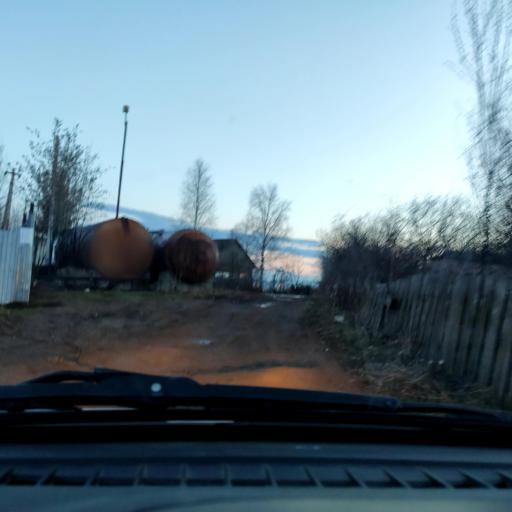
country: RU
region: Perm
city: Froly
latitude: 57.9405
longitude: 56.1971
